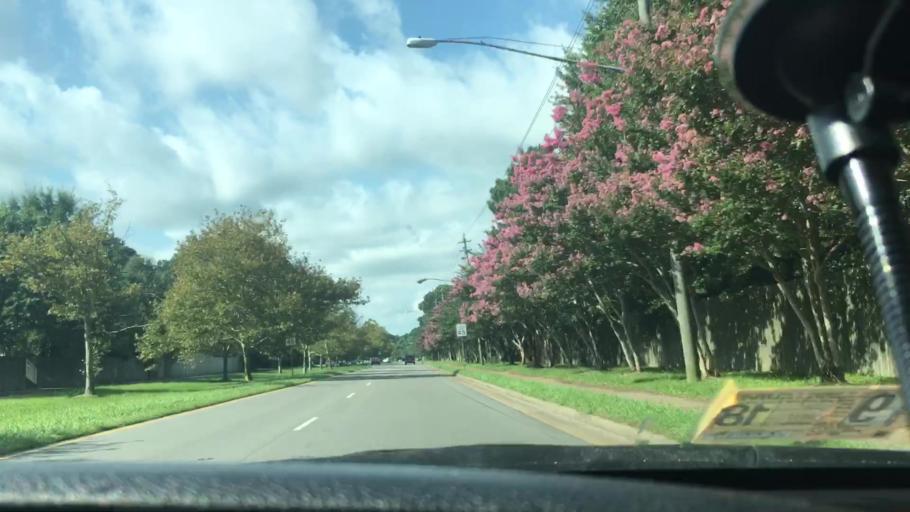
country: US
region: Virginia
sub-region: City of Virginia Beach
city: Virginia Beach
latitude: 36.8694
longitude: -76.0420
